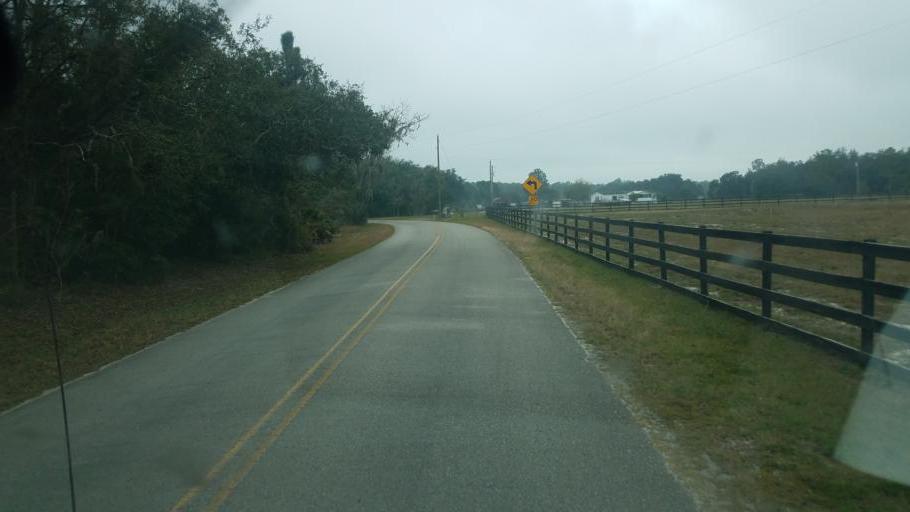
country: US
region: Florida
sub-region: Lake County
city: Groveland
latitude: 28.3846
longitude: -81.8503
